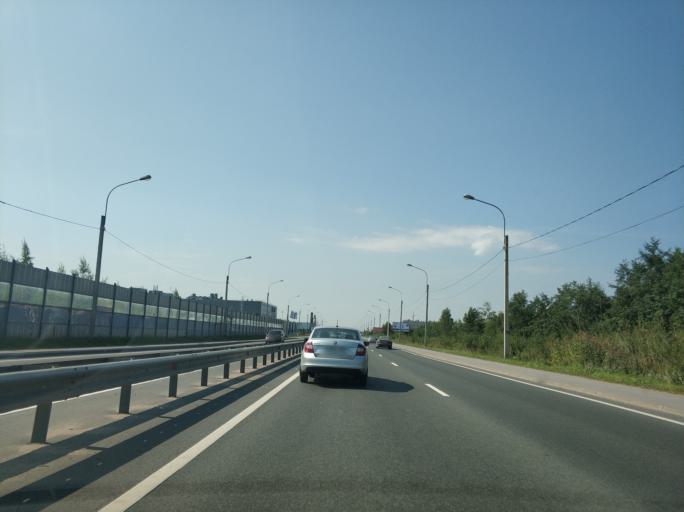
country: RU
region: Leningrad
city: Vsevolozhsk
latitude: 60.0296
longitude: 30.6230
